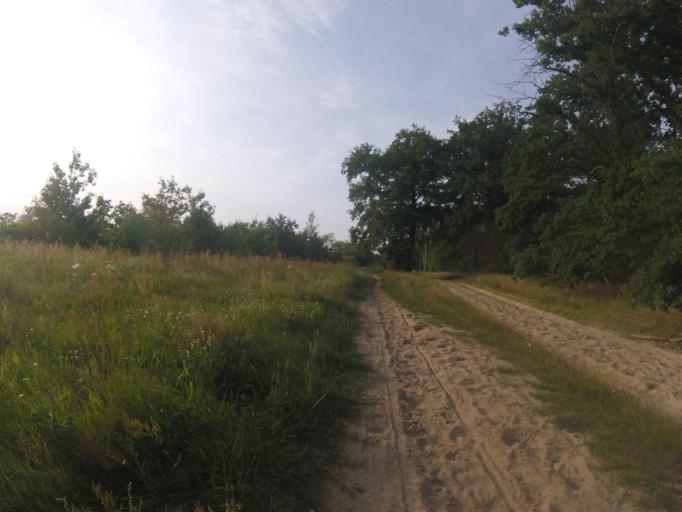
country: DE
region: Berlin
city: Lichtenrade
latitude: 52.3588
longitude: 13.4522
